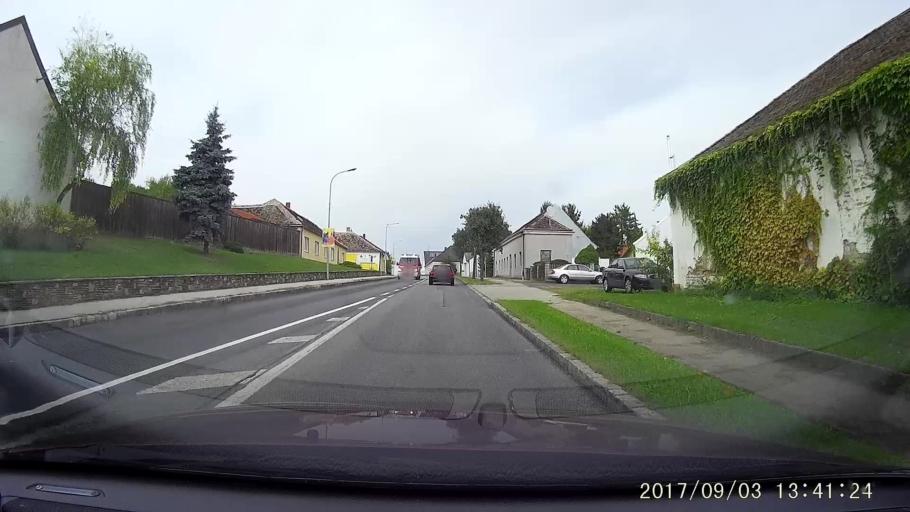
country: AT
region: Lower Austria
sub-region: Politischer Bezirk Hollabrunn
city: Wullersdorf
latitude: 48.6021
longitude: 16.0636
